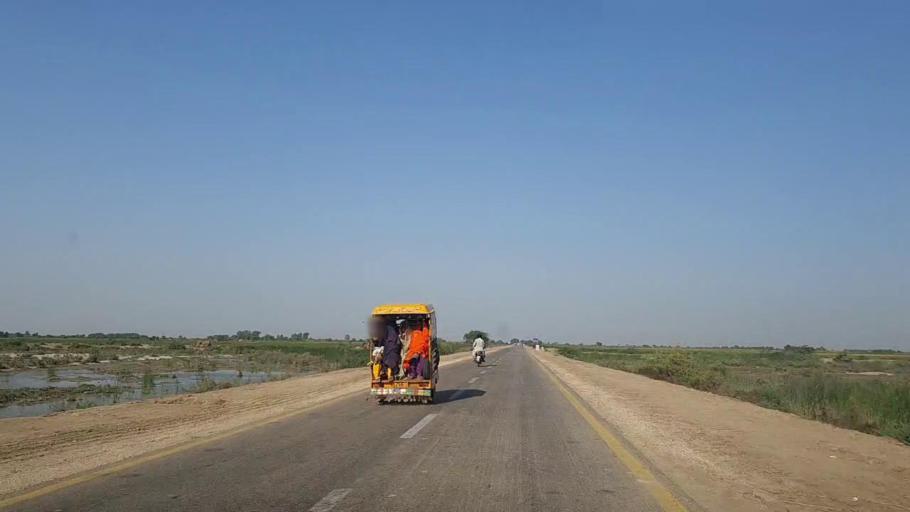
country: PK
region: Sindh
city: Jati
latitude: 24.4057
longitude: 68.2966
